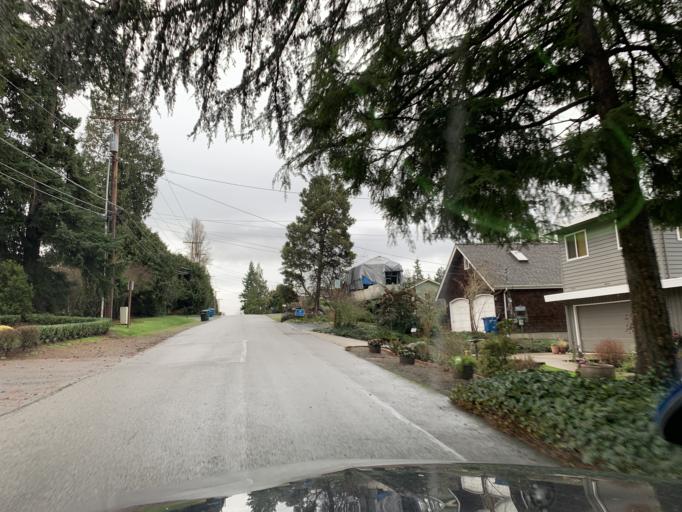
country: US
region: Washington
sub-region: King County
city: Mercer Island
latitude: 47.5915
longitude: -122.2336
